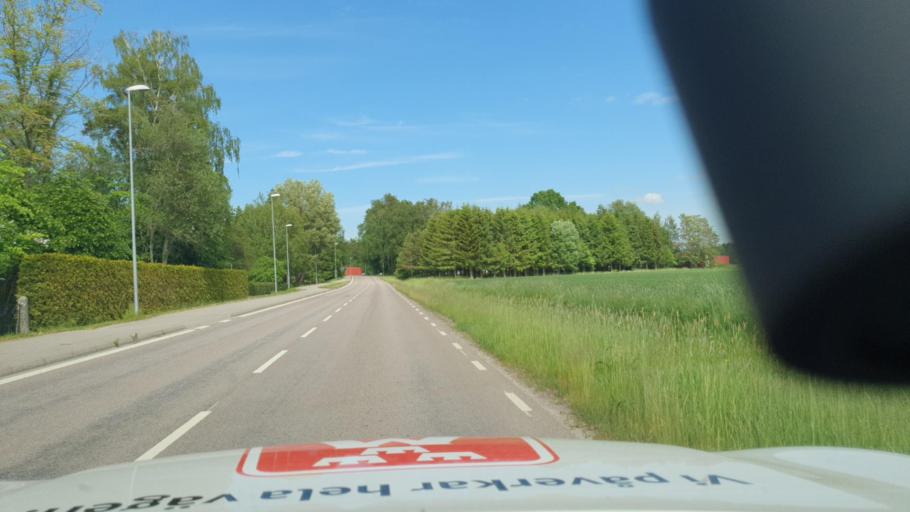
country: SE
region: Vaestra Goetaland
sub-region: Essunga Kommun
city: Nossebro
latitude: 58.2332
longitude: 12.6673
